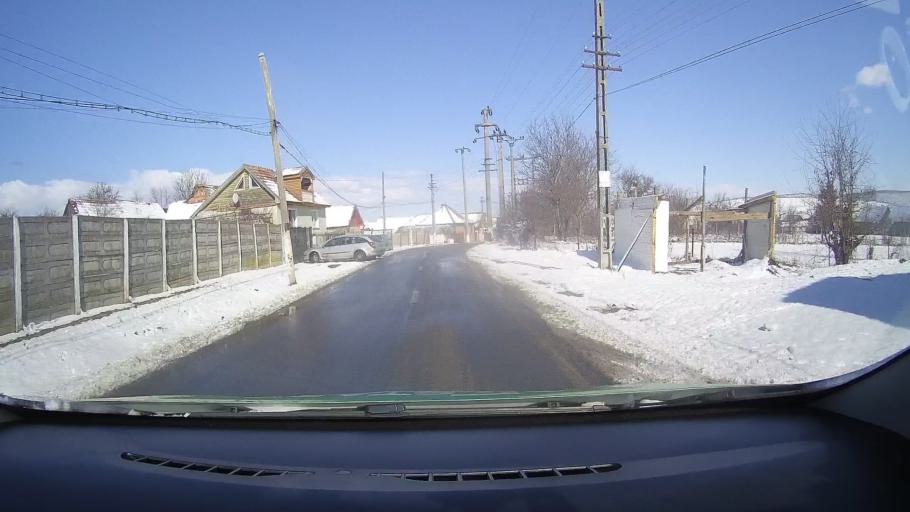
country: RO
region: Sibiu
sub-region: Comuna Rosia
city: Rosia
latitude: 45.8172
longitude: 24.3096
